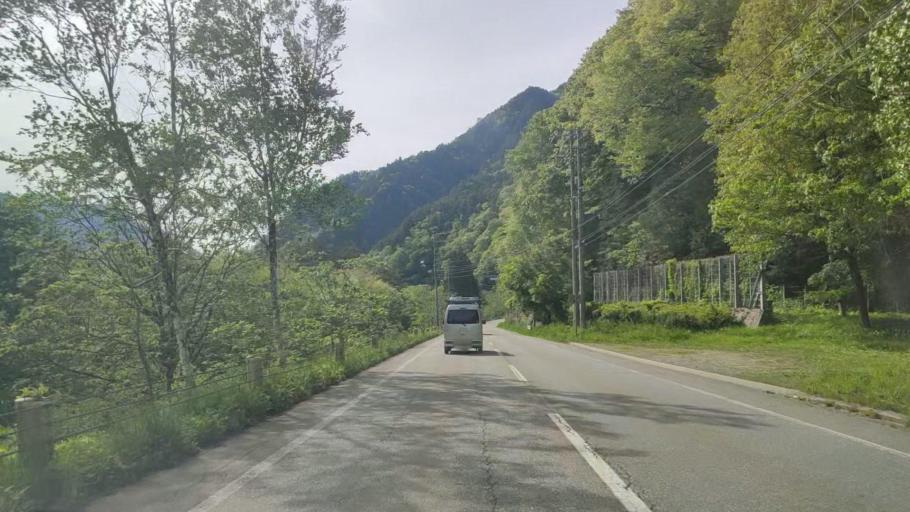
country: JP
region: Gifu
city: Takayama
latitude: 36.2573
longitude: 137.4699
